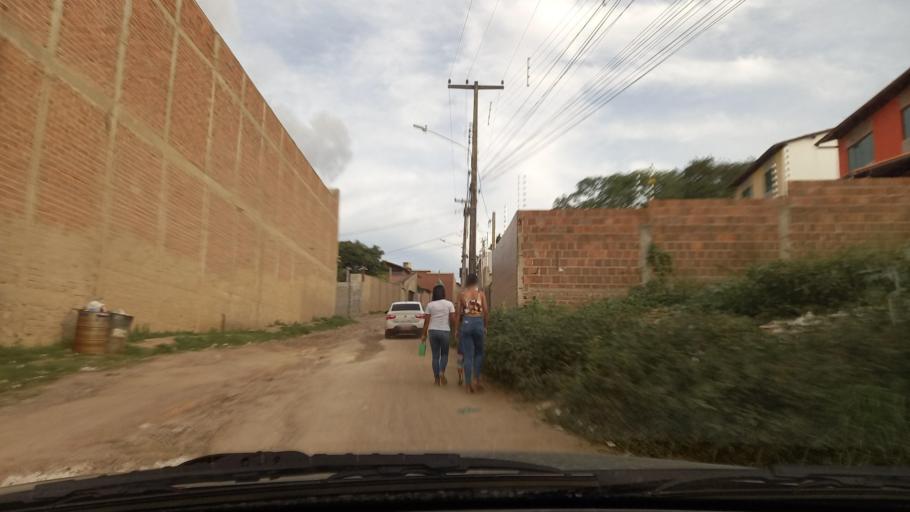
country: BR
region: Pernambuco
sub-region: Gravata
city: Gravata
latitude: -8.1926
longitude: -35.5703
